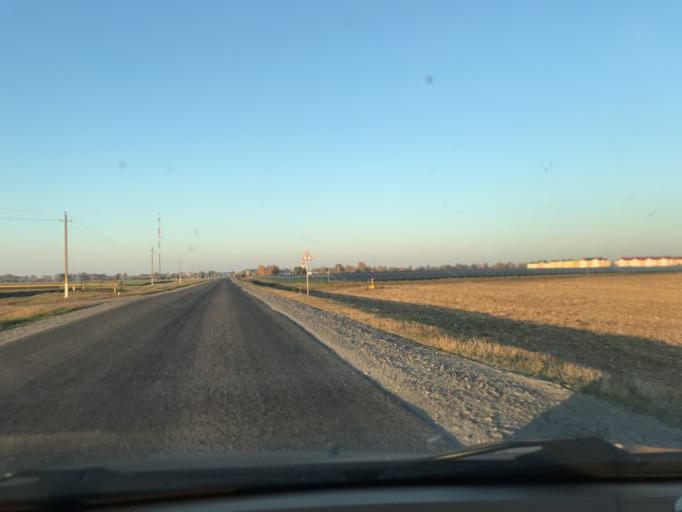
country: BY
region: Gomel
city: Brahin
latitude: 51.7810
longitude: 30.2523
